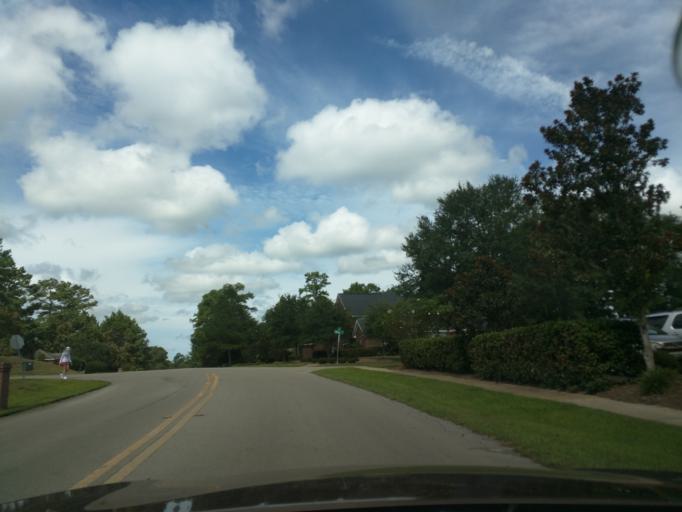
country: US
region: Florida
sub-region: Leon County
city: Tallahassee
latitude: 30.5697
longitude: -84.2587
